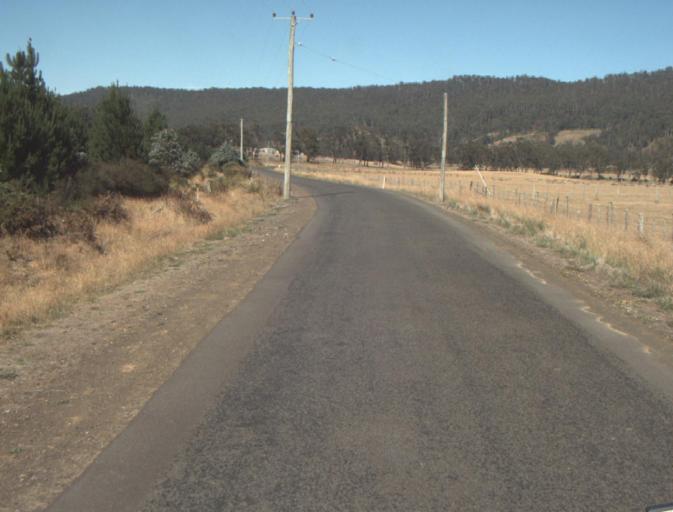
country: AU
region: Tasmania
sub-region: Launceston
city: Newstead
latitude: -41.3294
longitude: 147.3102
